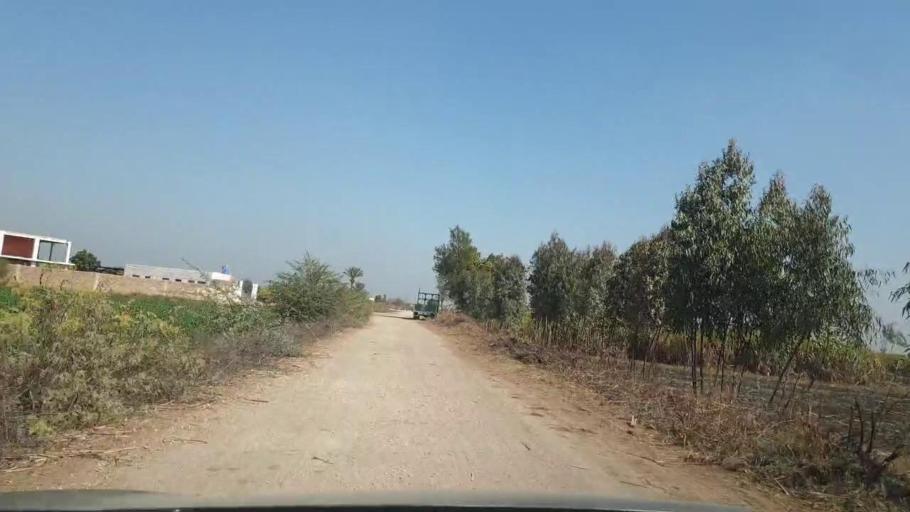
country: PK
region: Sindh
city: Tando Adam
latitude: 25.6284
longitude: 68.6484
